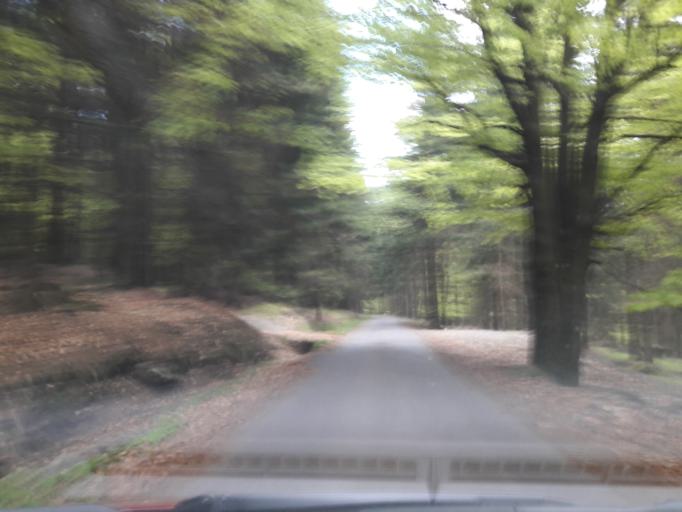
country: CZ
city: Machov
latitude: 50.4680
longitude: 16.2925
